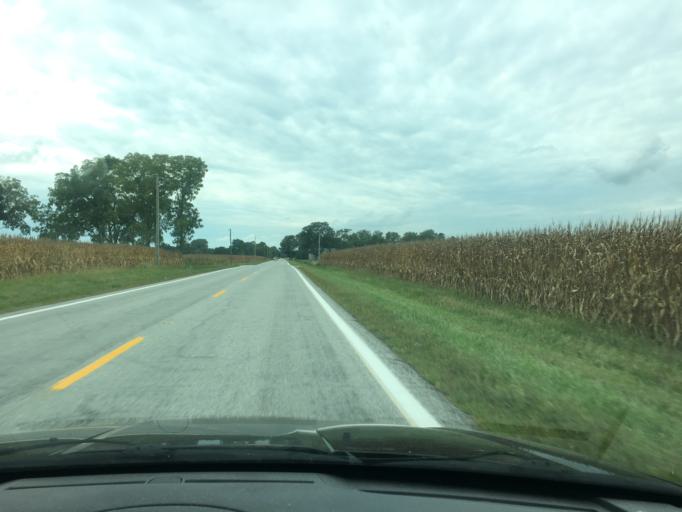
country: US
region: Ohio
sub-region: Champaign County
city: Urbana
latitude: 40.1561
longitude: -83.7581
